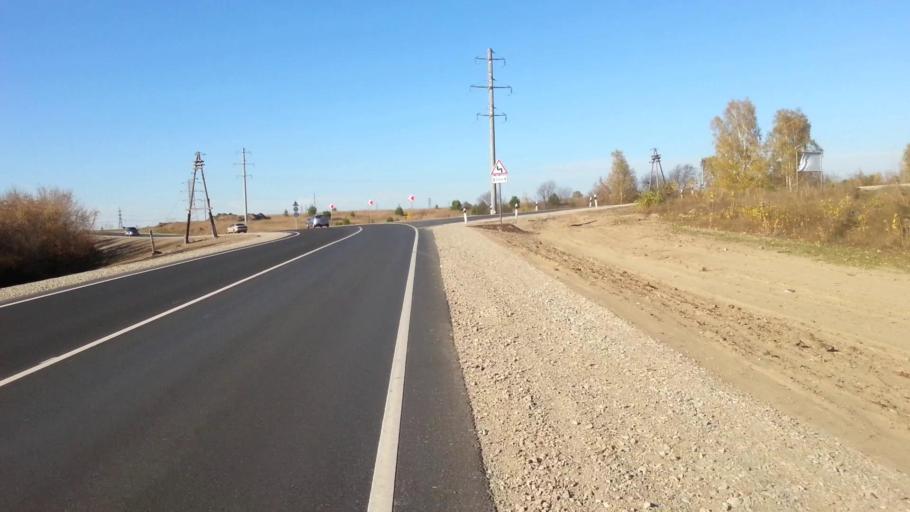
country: RU
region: Altai Krai
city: Sannikovo
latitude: 53.3277
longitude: 83.9413
